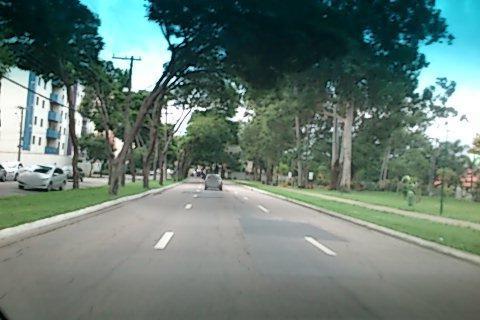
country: BR
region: Sao Paulo
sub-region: Sao Jose Dos Campos
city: Sao Jose dos Campos
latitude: -23.2383
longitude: -45.8809
